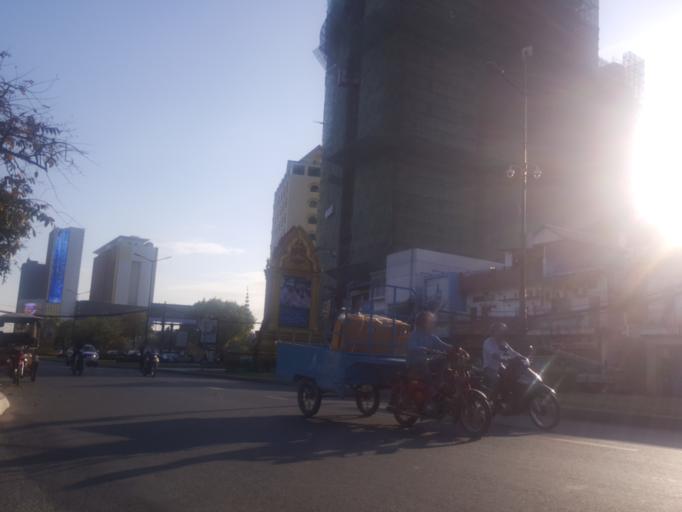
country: KH
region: Phnom Penh
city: Phnom Penh
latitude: 11.5612
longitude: 104.9353
